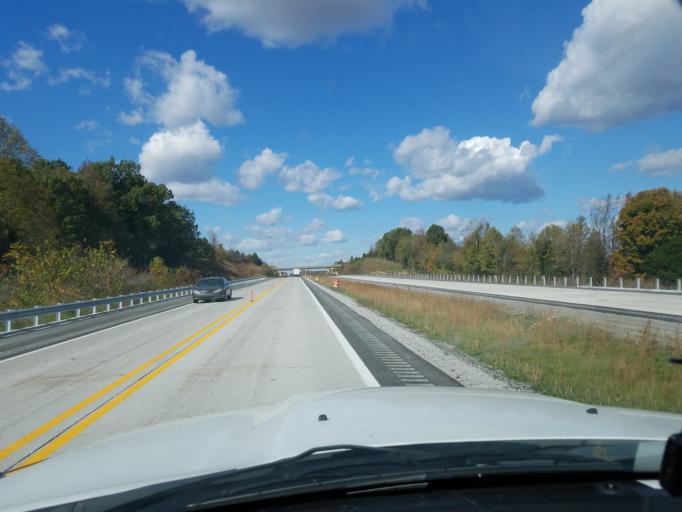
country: US
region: Kentucky
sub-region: Ohio County
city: Beaver Dam
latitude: 37.4331
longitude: -86.8490
